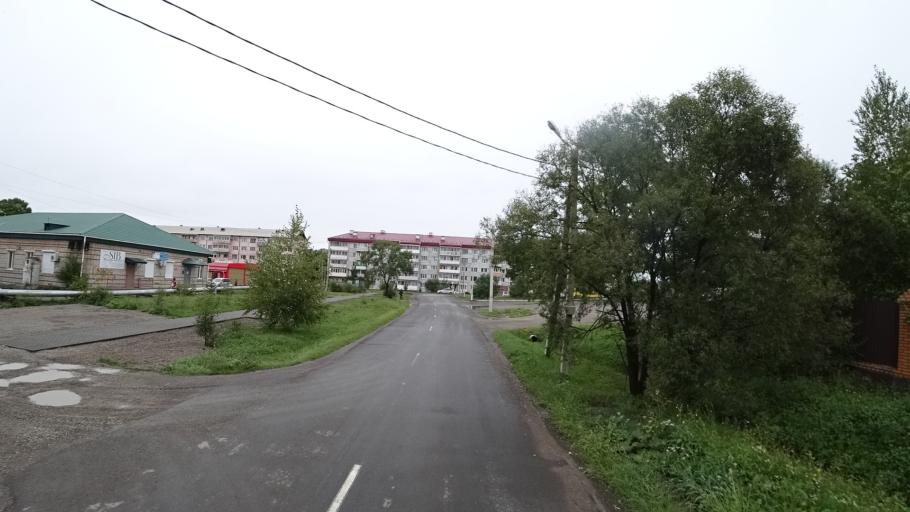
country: RU
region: Primorskiy
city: Monastyrishche
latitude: 44.2028
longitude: 132.4479
